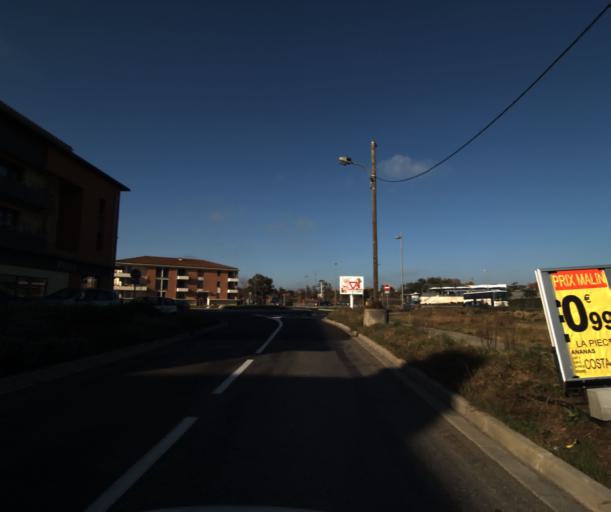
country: FR
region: Midi-Pyrenees
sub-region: Departement de la Haute-Garonne
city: Colomiers
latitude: 43.6014
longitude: 1.3539
